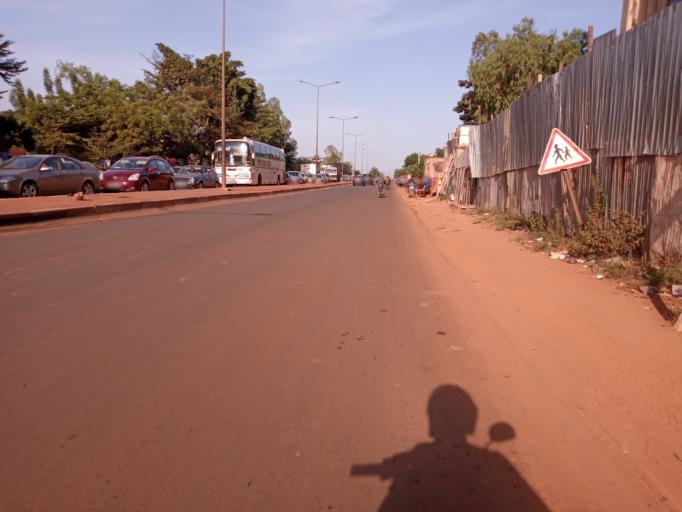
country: ML
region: Bamako
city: Bamako
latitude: 12.6141
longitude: -7.9918
